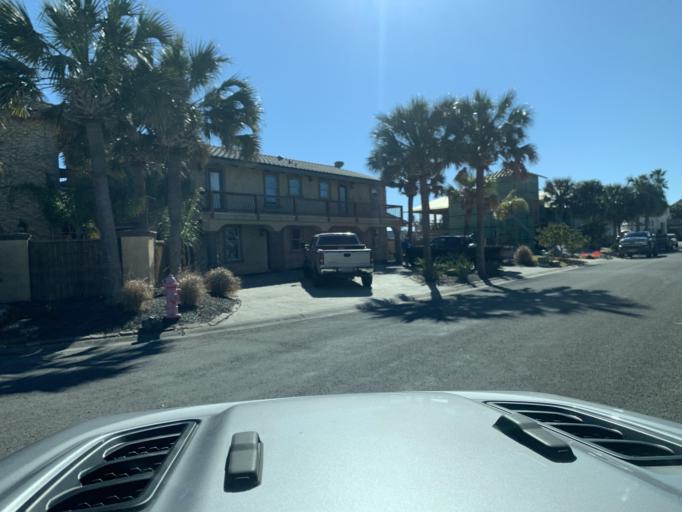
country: US
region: Texas
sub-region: Aransas County
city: Fulton
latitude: 28.0334
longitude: -97.0271
